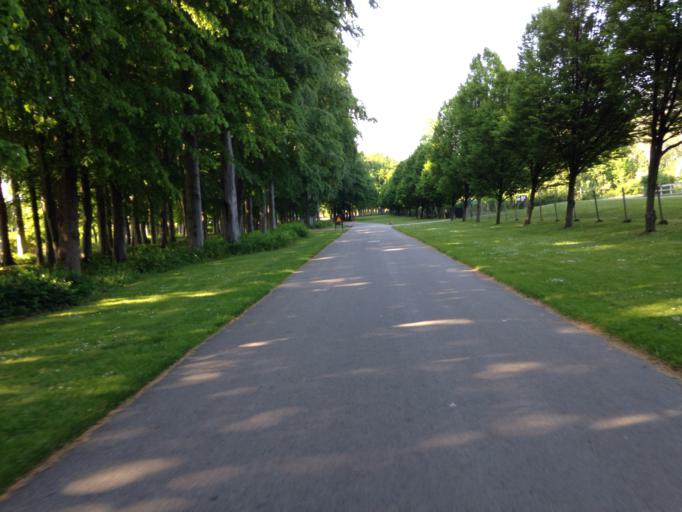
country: SE
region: Skane
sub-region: Burlovs Kommun
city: Arloev
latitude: 55.5937
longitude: 13.0508
